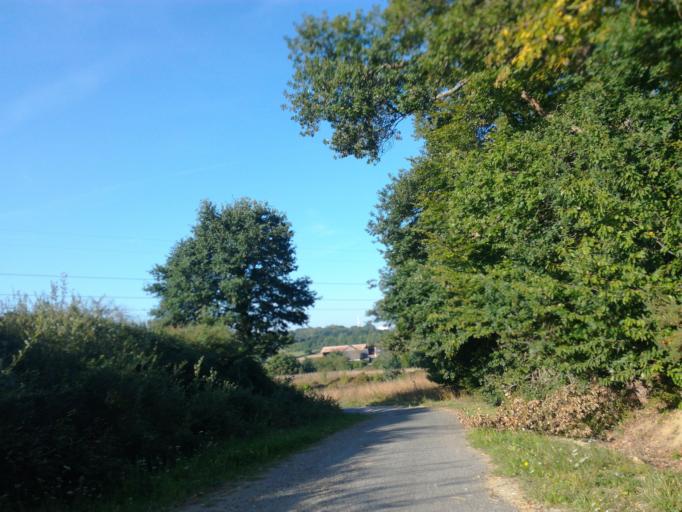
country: FR
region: Brittany
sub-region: Departement d'Ille-et-Vilaine
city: Fouillard
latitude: 48.1475
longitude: -1.5914
